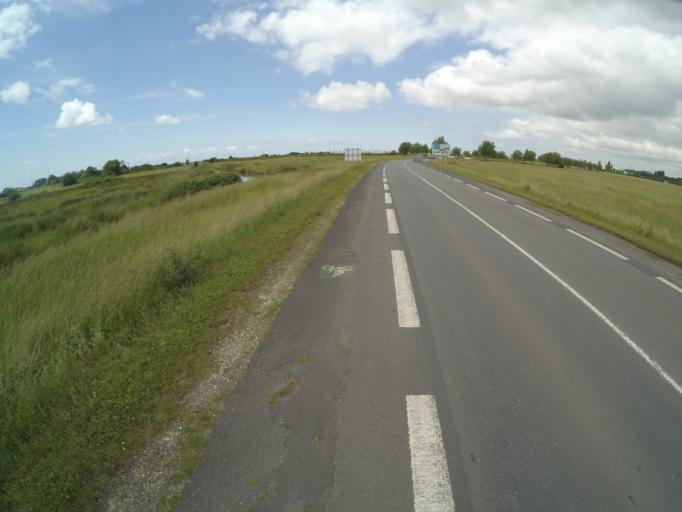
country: FR
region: Poitou-Charentes
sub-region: Departement de la Charente-Maritime
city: Rochefort
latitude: 45.9217
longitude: -0.9678
